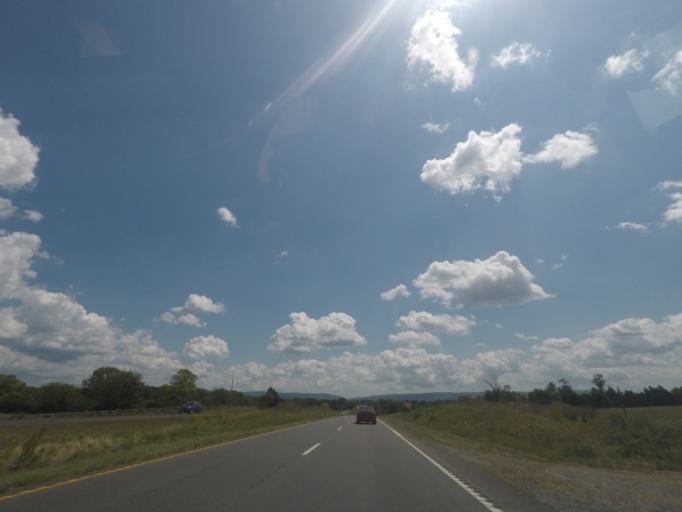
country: US
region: Virginia
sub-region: Warren County
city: Shenandoah Farms
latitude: 39.0866
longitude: -78.0901
